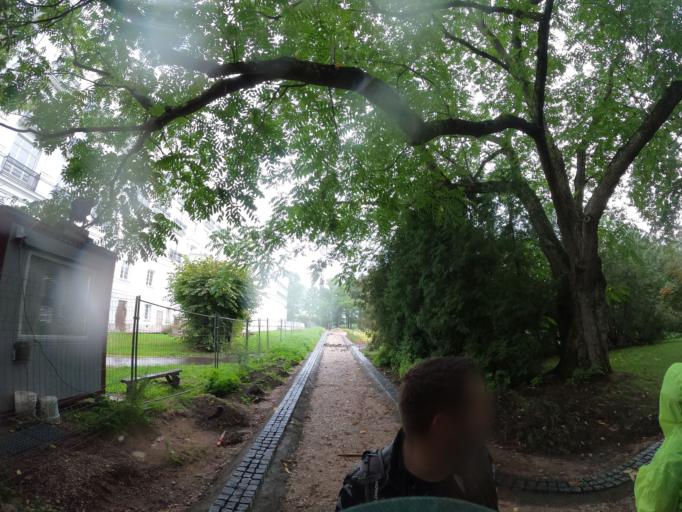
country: LV
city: Tireli
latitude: 56.9493
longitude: 23.4984
